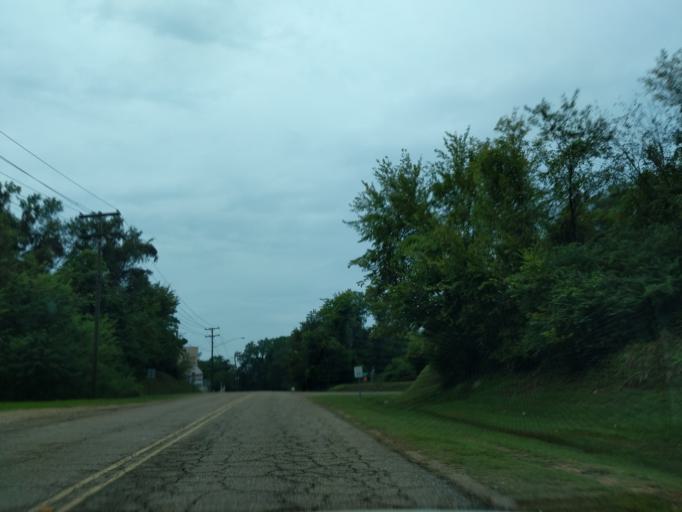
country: US
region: Mississippi
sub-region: Warren County
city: Vicksburg
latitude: 32.3175
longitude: -90.8881
